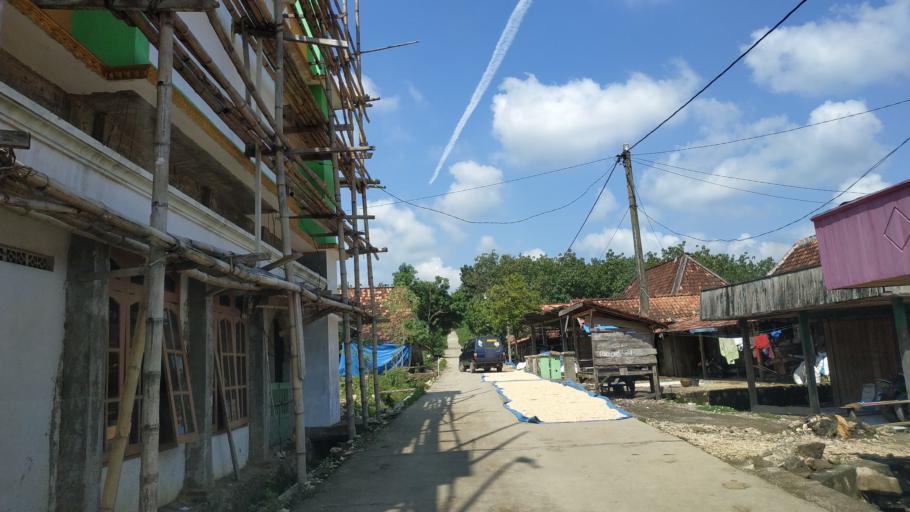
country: ID
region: Central Java
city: Guyangan
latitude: -7.0042
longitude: 111.0921
